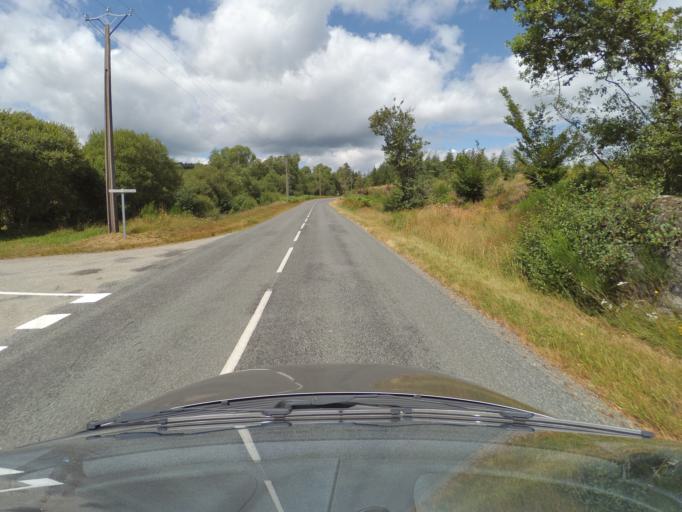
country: FR
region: Limousin
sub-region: Departement de la Haute-Vienne
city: Peyrat-le-Chateau
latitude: 45.8760
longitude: 1.8982
